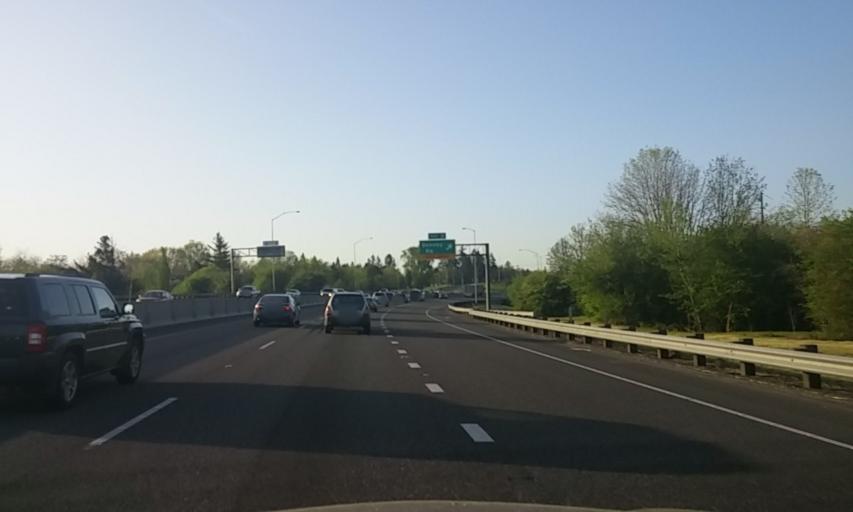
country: US
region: Oregon
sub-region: Washington County
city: Beaverton
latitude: 45.4733
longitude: -122.7870
